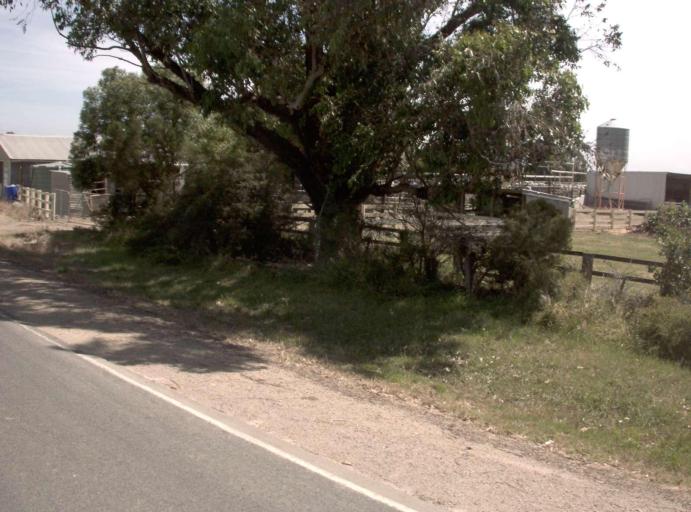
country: AU
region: Victoria
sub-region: Wellington
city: Heyfield
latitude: -38.0448
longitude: 146.8762
